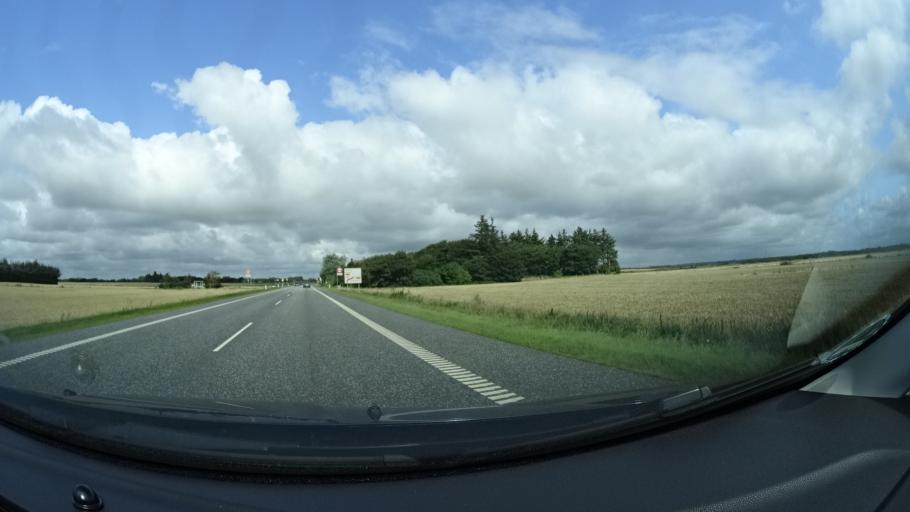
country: DK
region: Central Jutland
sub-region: Holstebro Kommune
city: Ulfborg
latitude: 56.2876
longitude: 8.3352
